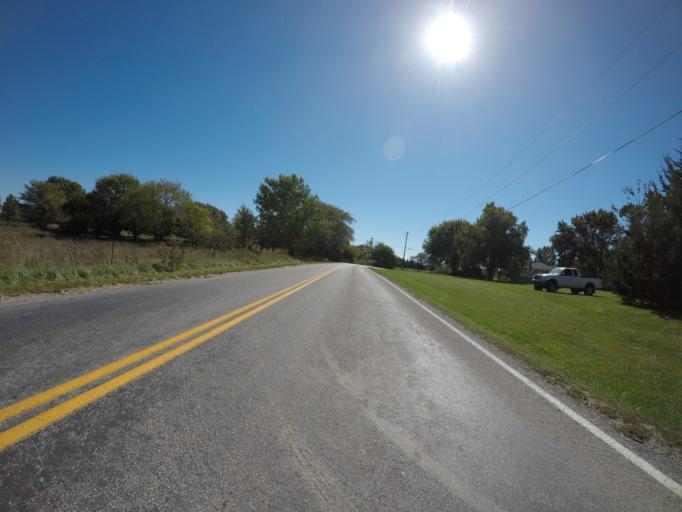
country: US
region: Kansas
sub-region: Wyandotte County
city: Bonner Springs
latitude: 39.0659
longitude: -94.9278
